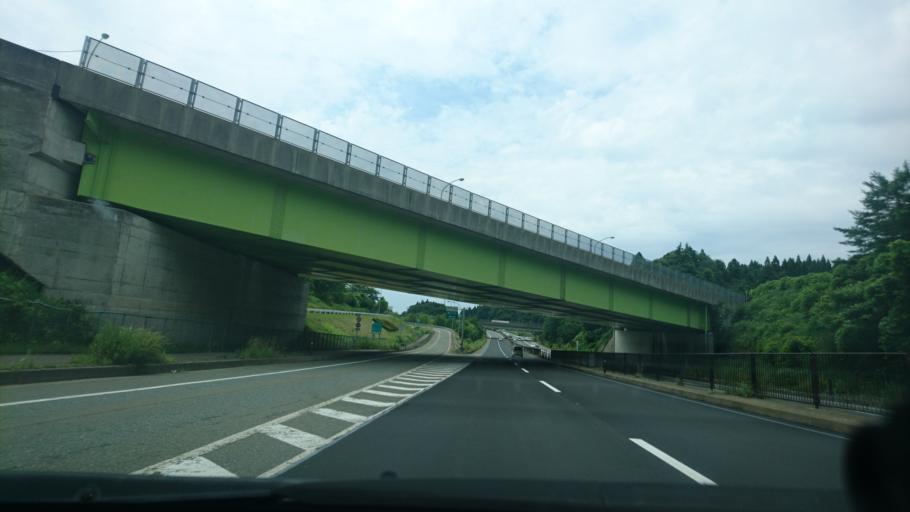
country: JP
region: Akita
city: Akita
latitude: 39.6612
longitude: 140.1907
